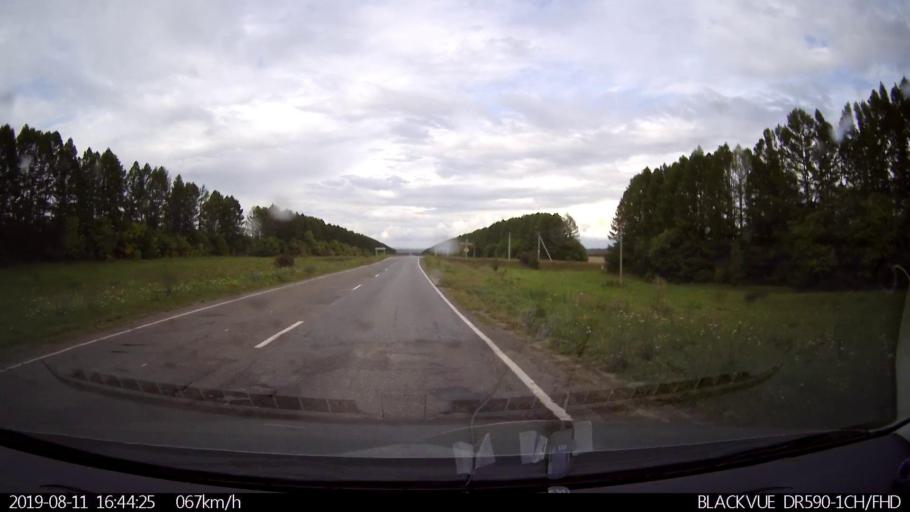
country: RU
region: Ulyanovsk
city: Mayna
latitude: 54.1788
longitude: 47.6797
